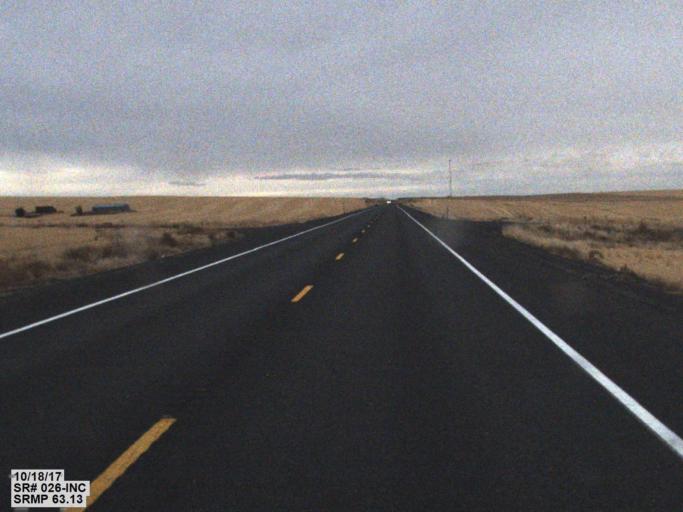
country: US
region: Washington
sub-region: Franklin County
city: Connell
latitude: 46.7944
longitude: -118.7047
